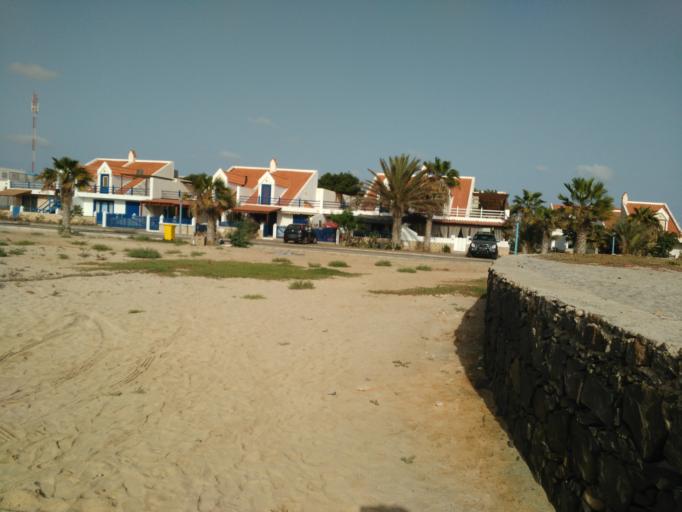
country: CV
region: Sal
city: Espargos
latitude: 16.6760
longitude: -22.9361
